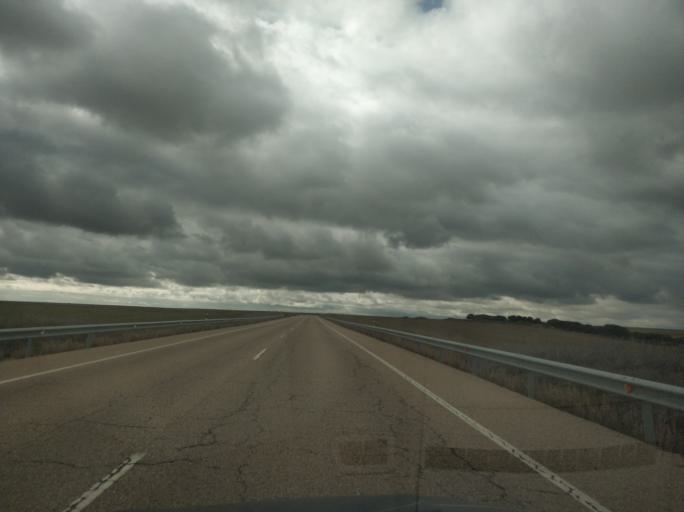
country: ES
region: Castille and Leon
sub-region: Provincia de Valladolid
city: Alaejos
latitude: 41.2732
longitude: -5.2550
